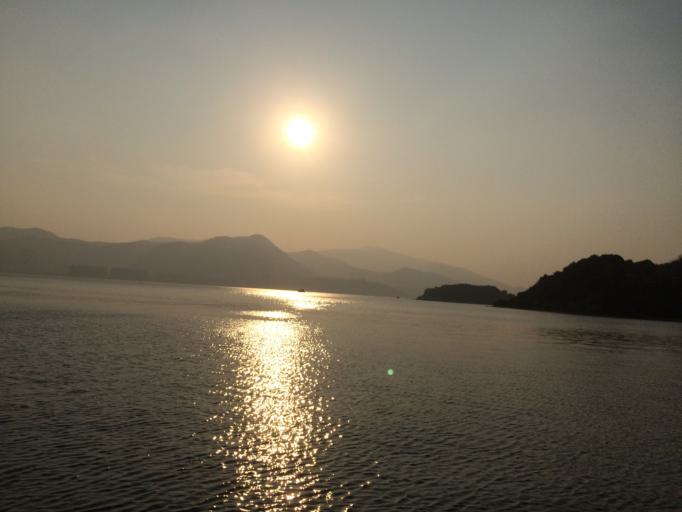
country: HK
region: Tai Po
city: Tai Po
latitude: 22.4498
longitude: 114.2246
